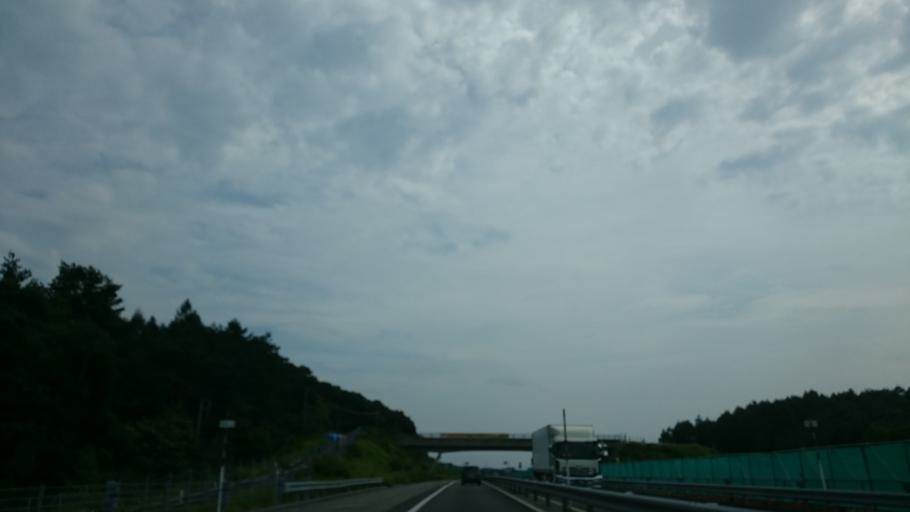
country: JP
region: Gifu
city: Gujo
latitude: 36.0080
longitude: 136.9292
